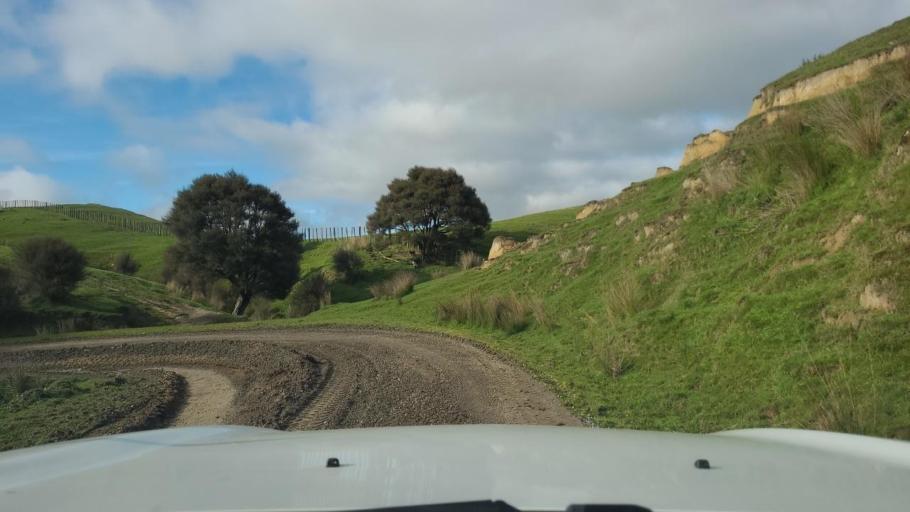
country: NZ
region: Wellington
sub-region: South Wairarapa District
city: Waipawa
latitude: -41.2427
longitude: 175.6879
